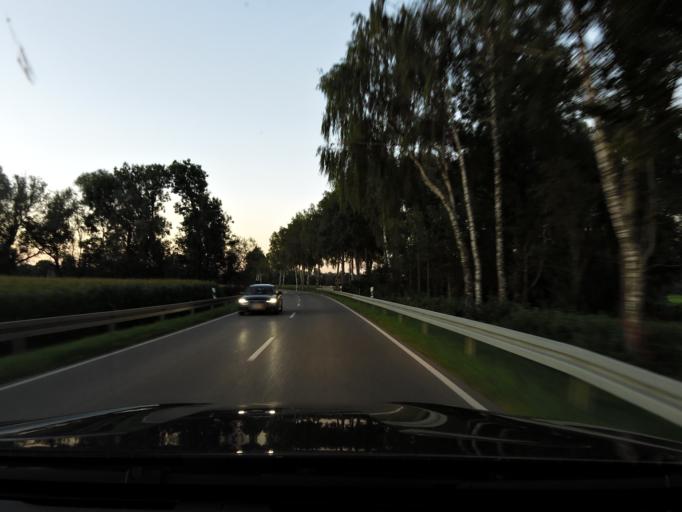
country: DE
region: Bavaria
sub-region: Upper Bavaria
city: Berglern
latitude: 48.4164
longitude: 11.9331
